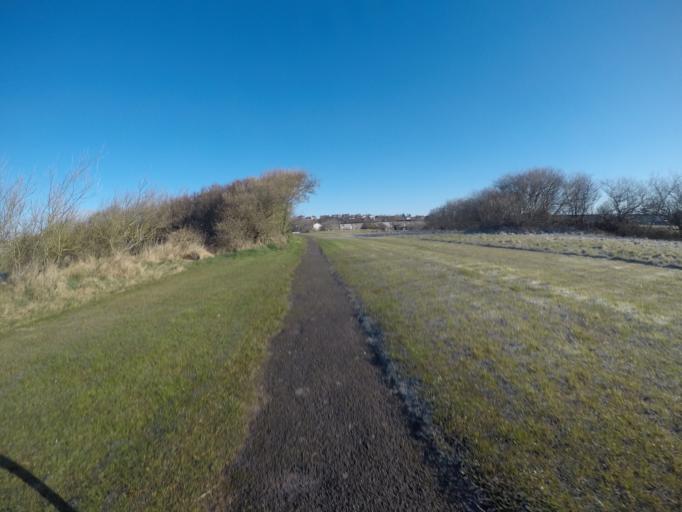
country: GB
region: Scotland
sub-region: North Ayrshire
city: Stevenston
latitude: 55.6364
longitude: -4.7630
